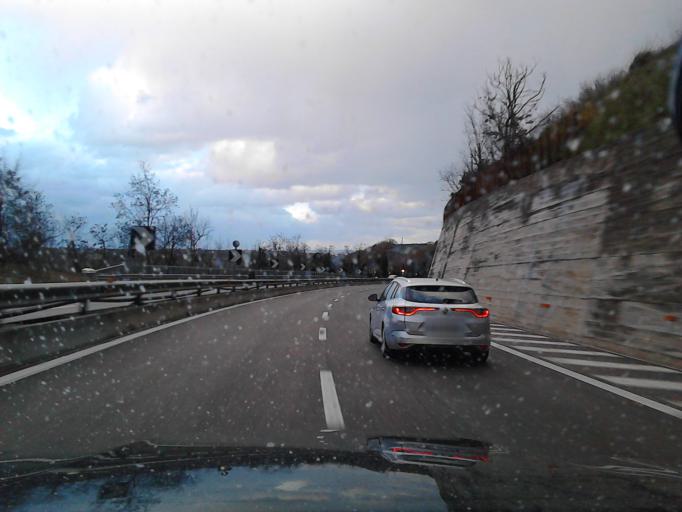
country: IT
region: Abruzzo
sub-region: Provincia di Chieti
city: Treglio
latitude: 42.2706
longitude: 14.4341
